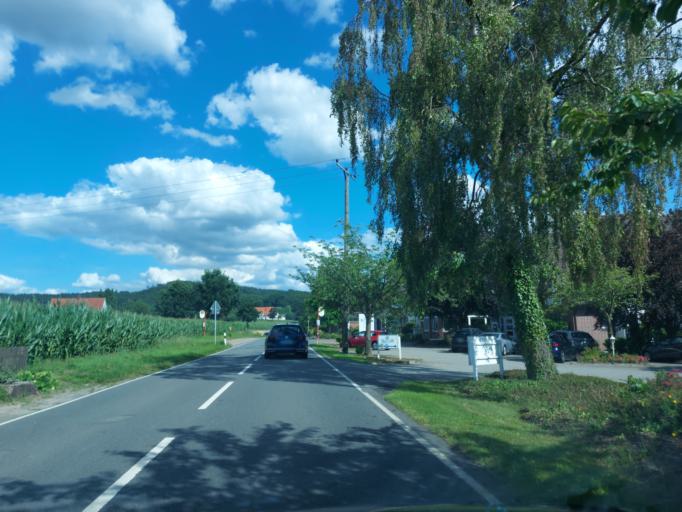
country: DE
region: Lower Saxony
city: Hagen
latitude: 52.1830
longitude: 7.9956
